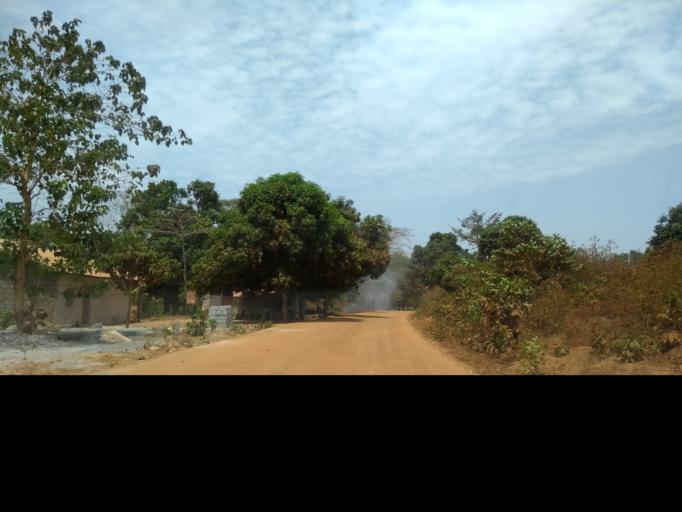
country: GN
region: Kindia
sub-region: Prefecture de Dubreka
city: Dubreka
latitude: 9.7874
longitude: -13.5356
